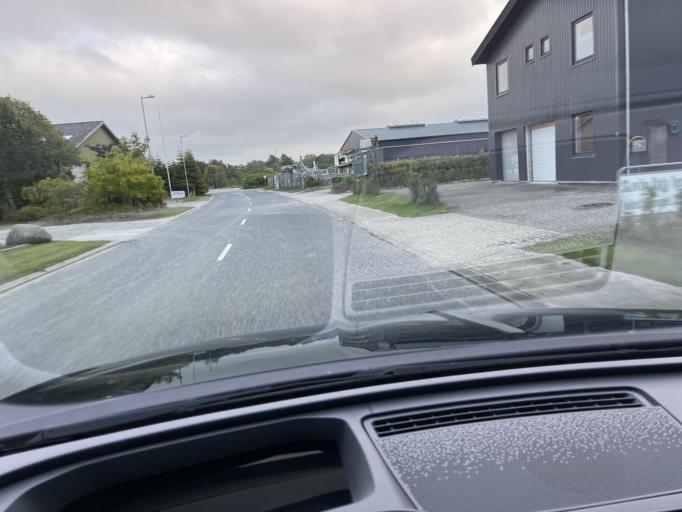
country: DK
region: Zealand
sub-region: Solrod Kommune
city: Havdrup
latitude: 55.5503
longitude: 12.1256
